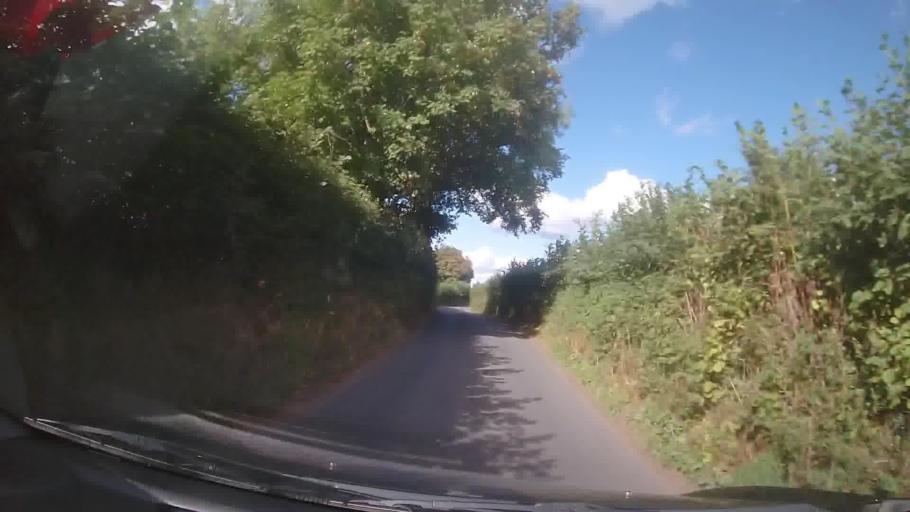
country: GB
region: Wales
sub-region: Sir Powys
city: Brecon
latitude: 51.8909
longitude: -3.2997
